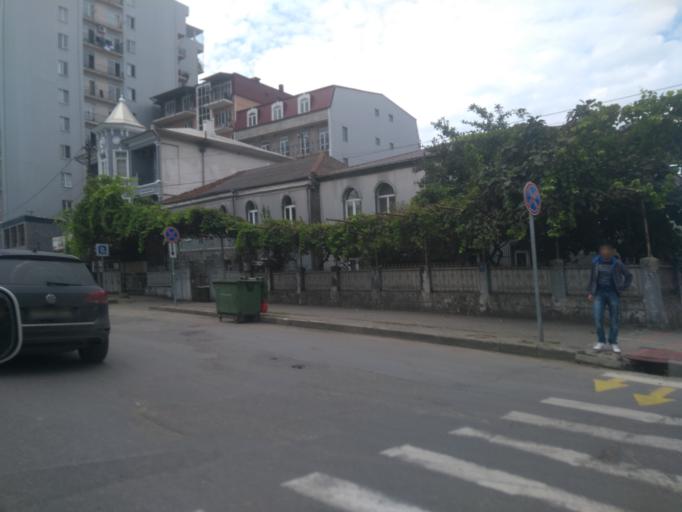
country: GE
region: Ajaria
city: Batumi
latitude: 41.6350
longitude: 41.6270
